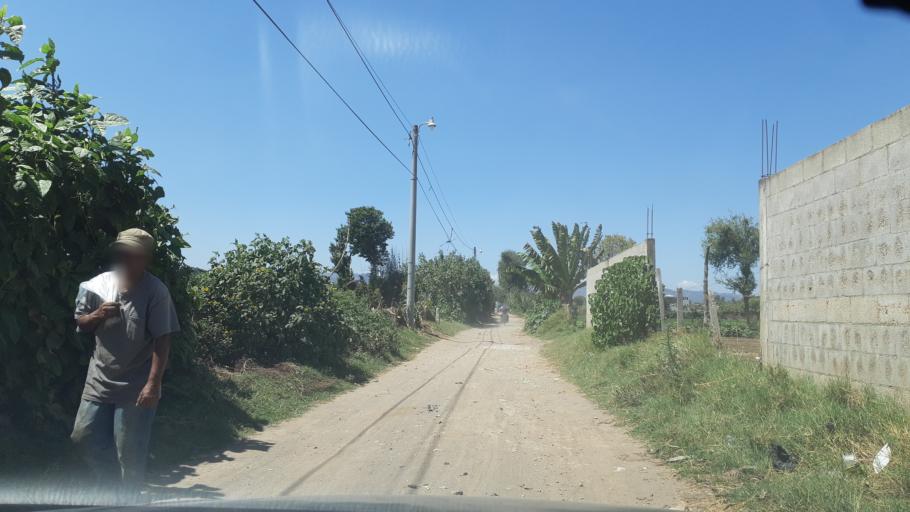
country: GT
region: Chimaltenango
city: El Tejar
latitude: 14.6448
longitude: -90.8080
